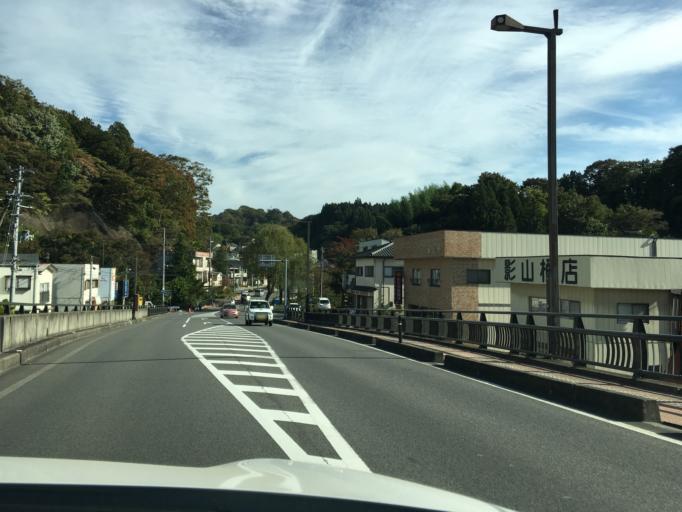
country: JP
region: Fukushima
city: Miharu
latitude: 37.4481
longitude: 140.4855
